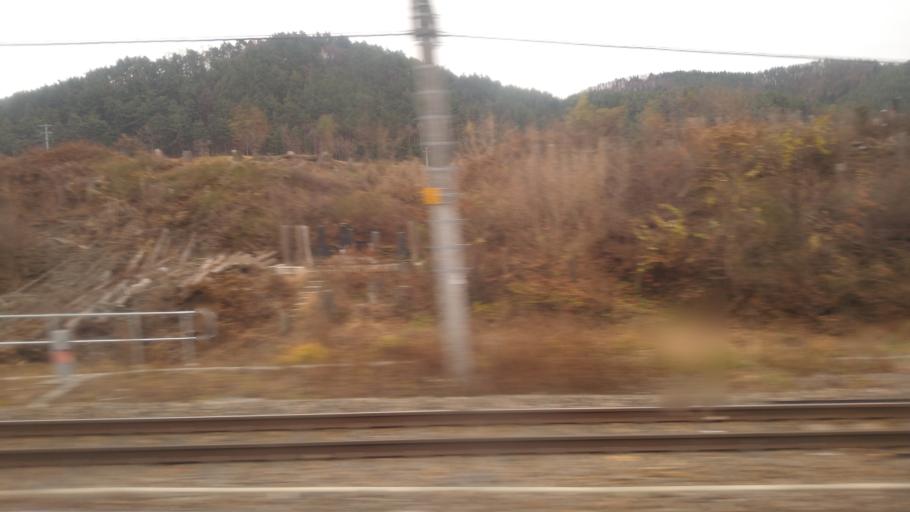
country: JP
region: Nagano
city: Shiojiri
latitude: 36.0885
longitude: 137.9181
